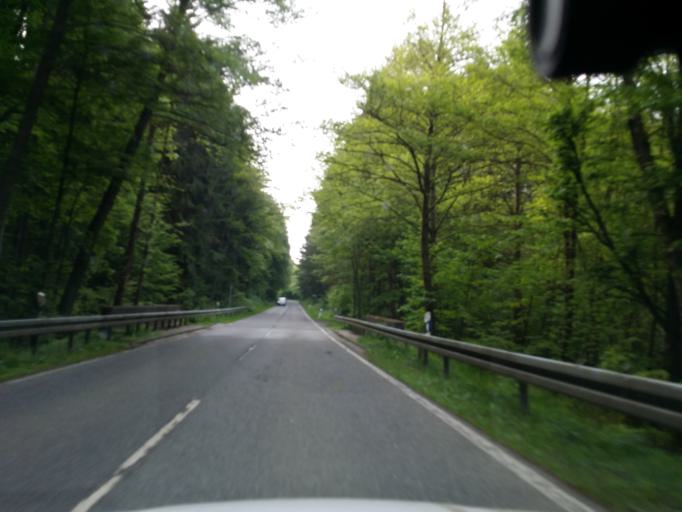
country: DE
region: Hesse
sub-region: Regierungsbezirk Darmstadt
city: Niedernhausen
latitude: 50.1900
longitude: 8.3523
